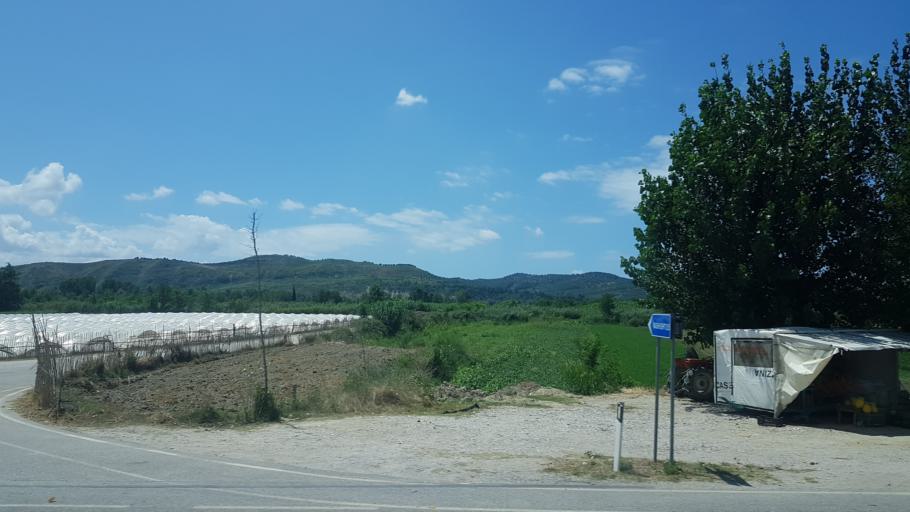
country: AL
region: Fier
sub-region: Rrethi i Fierit
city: Frakulla e Madhe
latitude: 40.6101
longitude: 19.5286
